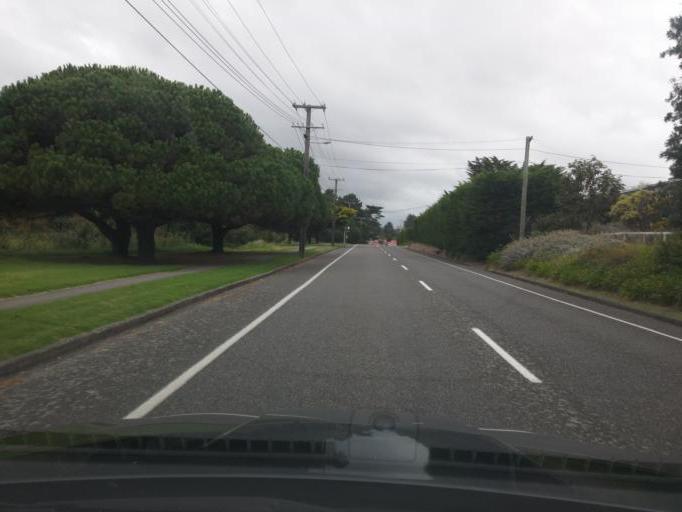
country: NZ
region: Wellington
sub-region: Kapiti Coast District
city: Paraparaumu
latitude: -40.8619
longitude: 175.0290
